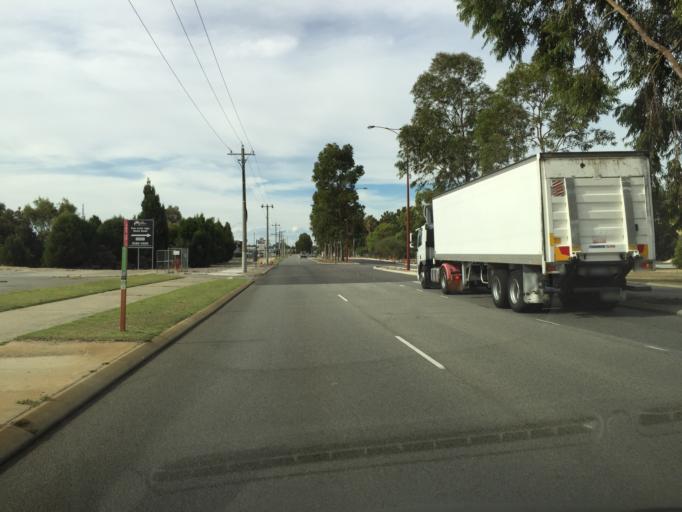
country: AU
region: Western Australia
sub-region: Canning
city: Canning Vale
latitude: -32.0645
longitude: 115.9018
